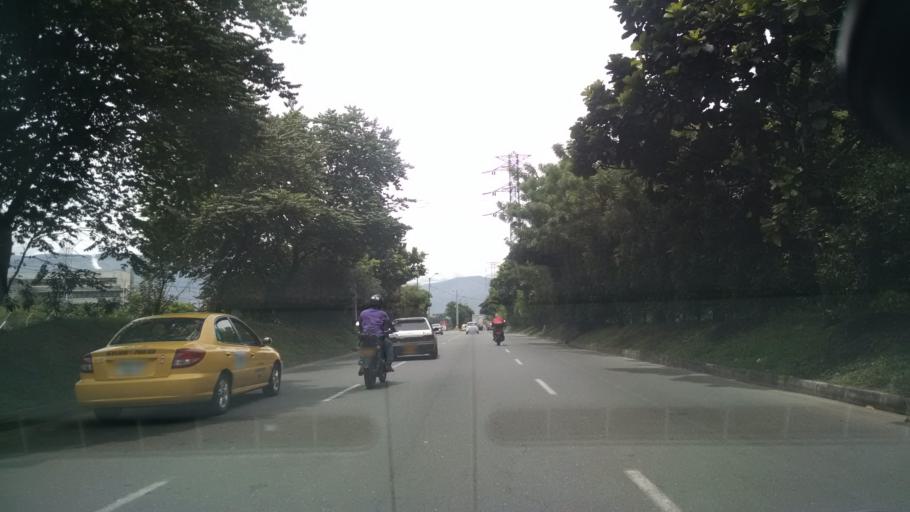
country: CO
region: Antioquia
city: Itagui
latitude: 6.2068
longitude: -75.5785
